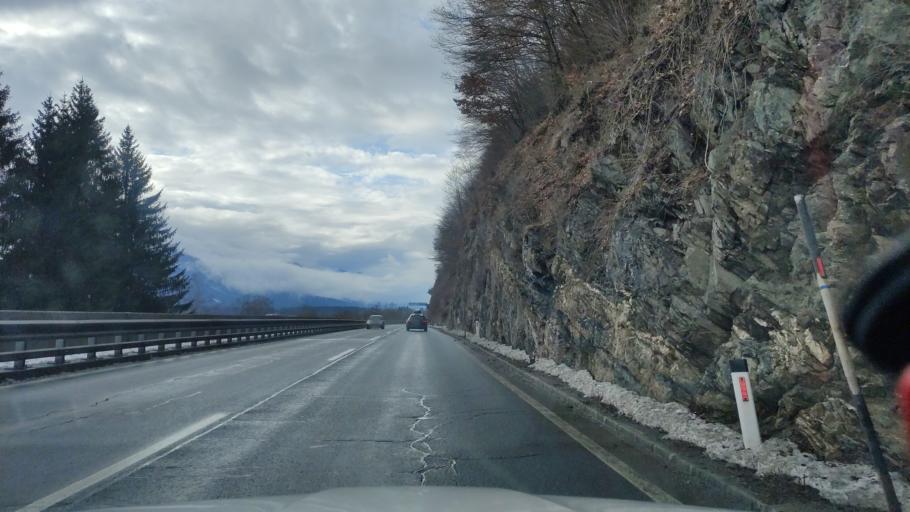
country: AT
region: Carinthia
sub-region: Politischer Bezirk Hermagor
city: Hermagor
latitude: 46.6220
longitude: 13.2960
